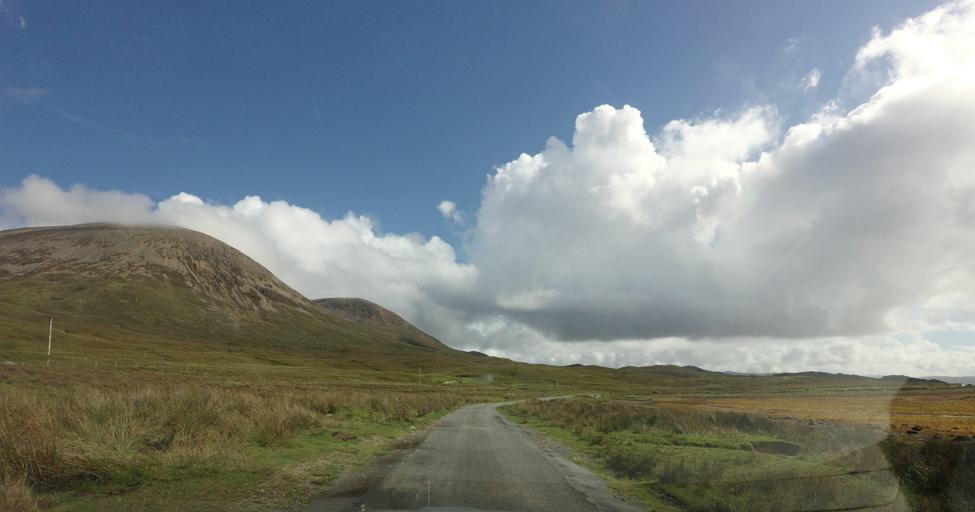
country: GB
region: Scotland
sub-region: Highland
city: Portree
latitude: 57.2257
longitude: -6.0323
